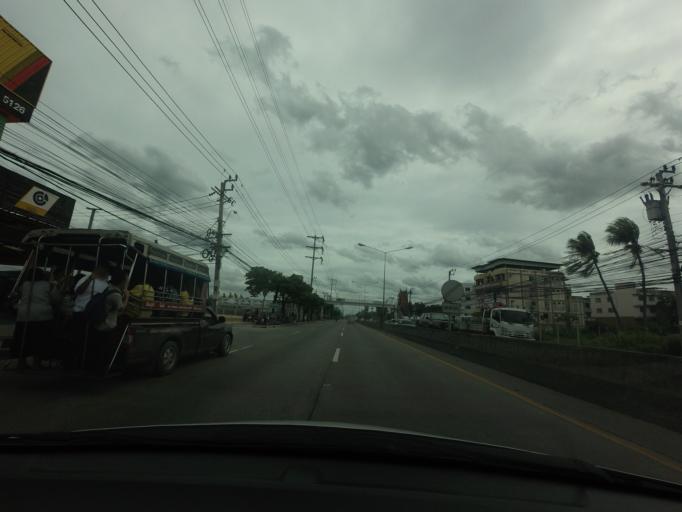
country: TH
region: Bangkok
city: Min Buri
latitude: 13.7785
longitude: 100.7465
